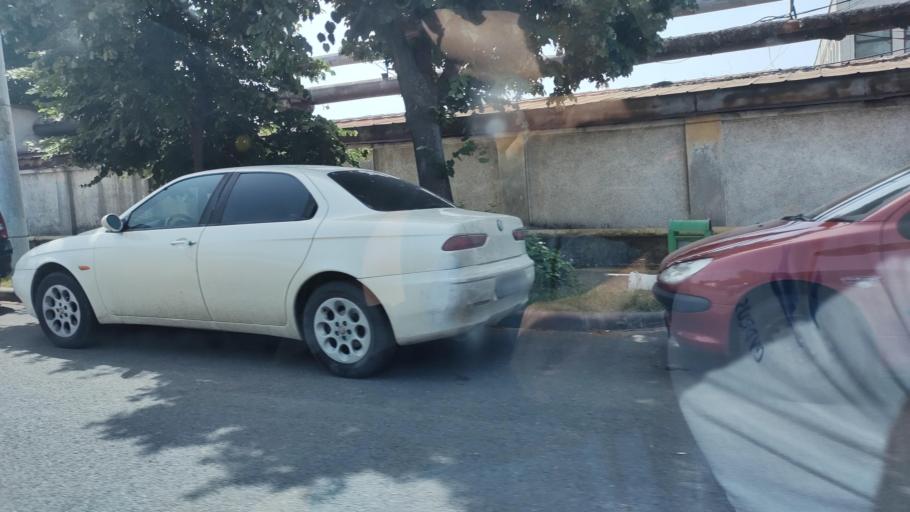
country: RO
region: Mehedinti
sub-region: Municipiul Drobeta-Turnu Severin
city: Drobeta-Turnu Severin
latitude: 44.6238
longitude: 22.6370
